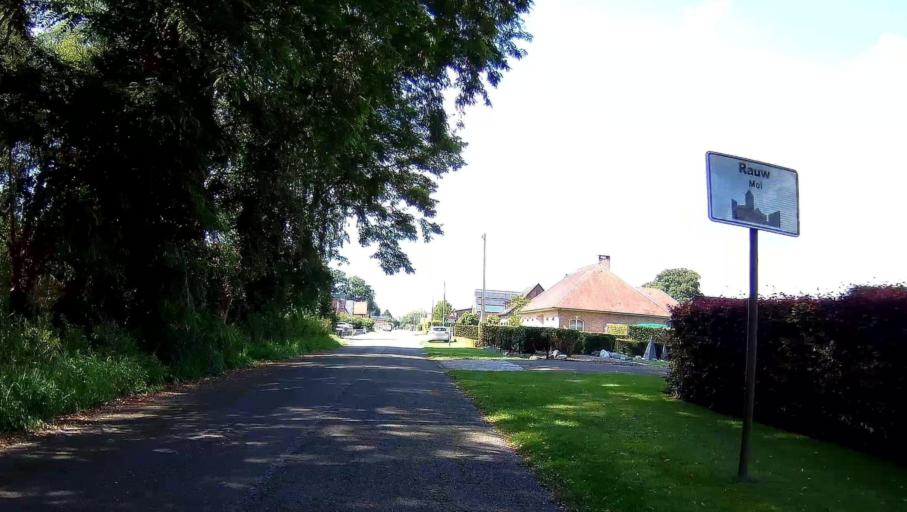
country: BE
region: Flanders
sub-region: Provincie Antwerpen
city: Balen
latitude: 51.2144
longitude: 5.2067
